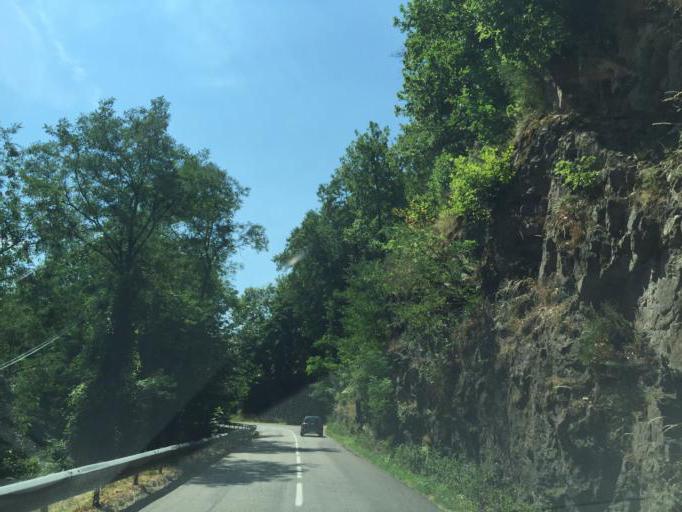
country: FR
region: Rhone-Alpes
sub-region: Departement de la Loire
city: Saint-Chamond
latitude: 45.4335
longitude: 4.5122
